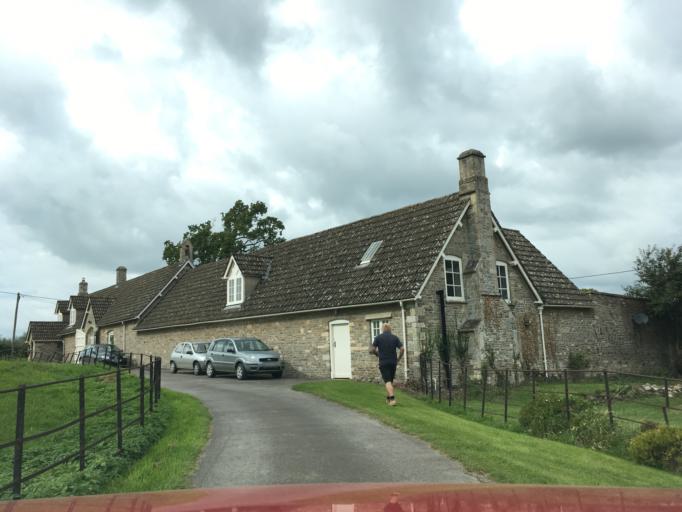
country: GB
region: England
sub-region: South Gloucestershire
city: Charfield
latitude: 51.6388
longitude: -2.4291
